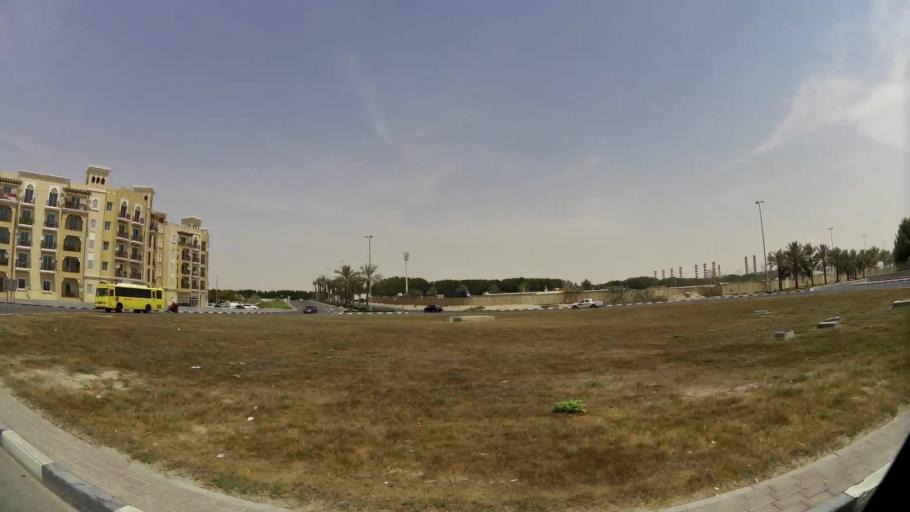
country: AE
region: Ash Shariqah
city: Sharjah
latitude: 25.1593
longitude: 55.4218
